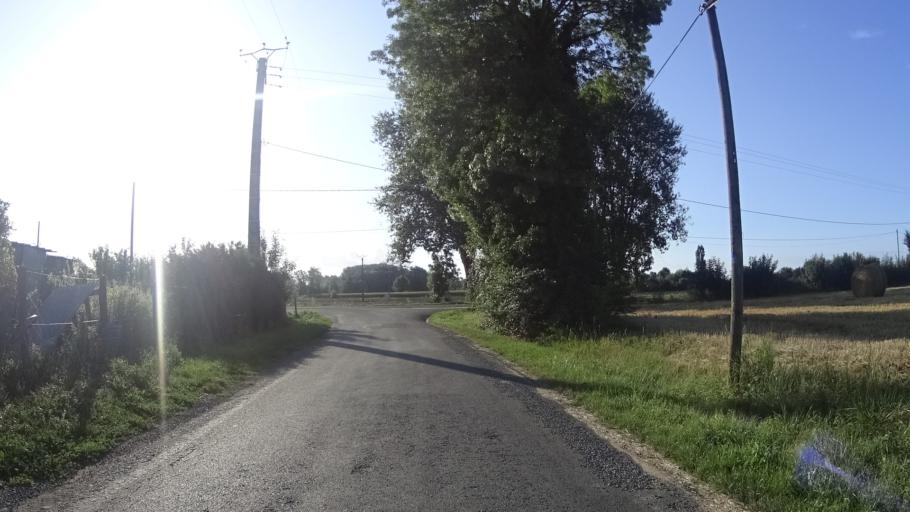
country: FR
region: Pays de la Loire
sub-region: Departement de Maine-et-Loire
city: Villebernier
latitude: 47.2717
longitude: -0.0130
